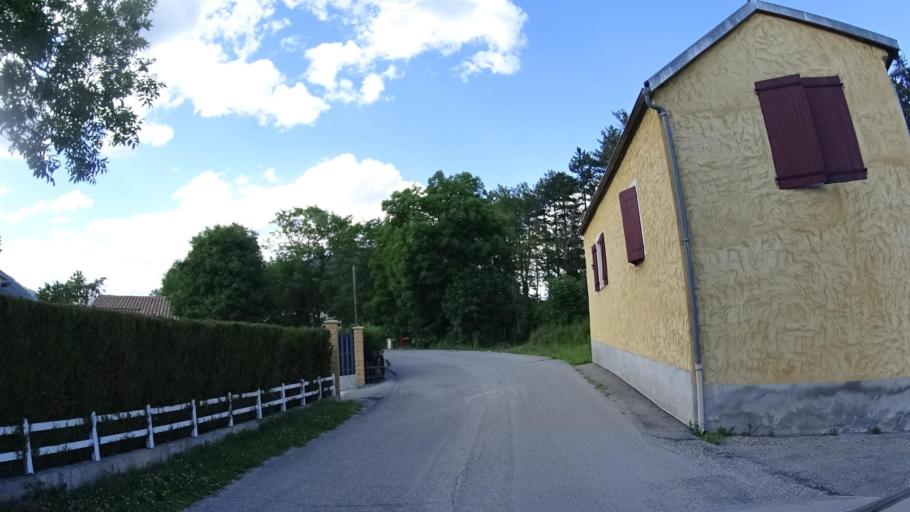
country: FR
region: Provence-Alpes-Cote d'Azur
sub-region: Departement des Alpes-de-Haute-Provence
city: Castellane
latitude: 43.9693
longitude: 6.5134
